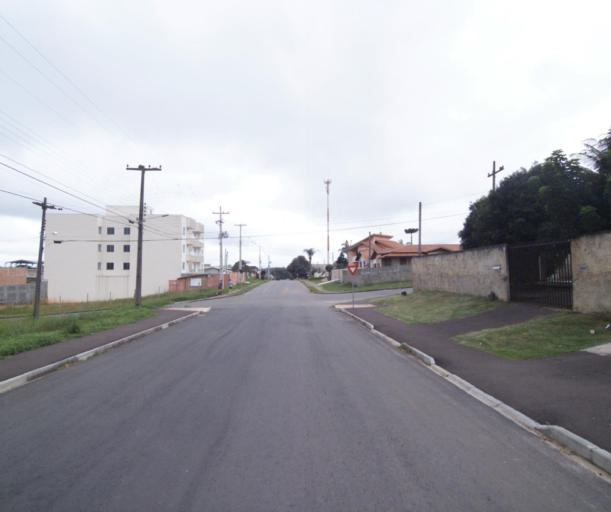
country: BR
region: Parana
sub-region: Quatro Barras
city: Quatro Barras
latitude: -25.3644
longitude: -49.1078
